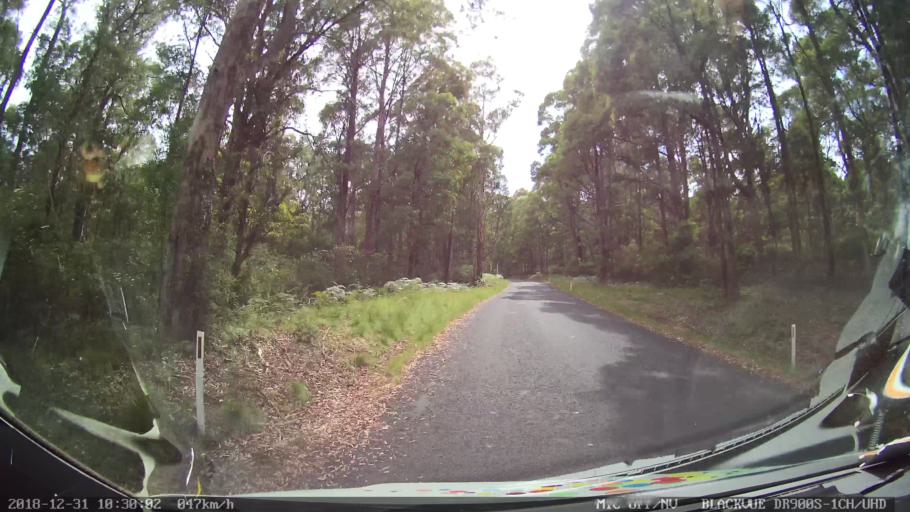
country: AU
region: New South Wales
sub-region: Snowy River
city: Jindabyne
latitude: -36.4657
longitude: 148.1492
